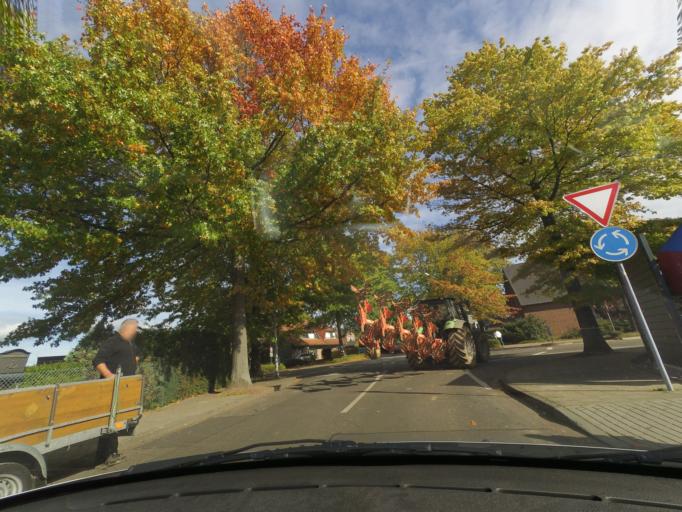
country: DE
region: North Rhine-Westphalia
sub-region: Regierungsbezirk Dusseldorf
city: Korschenbroich
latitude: 51.1478
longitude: 6.5480
